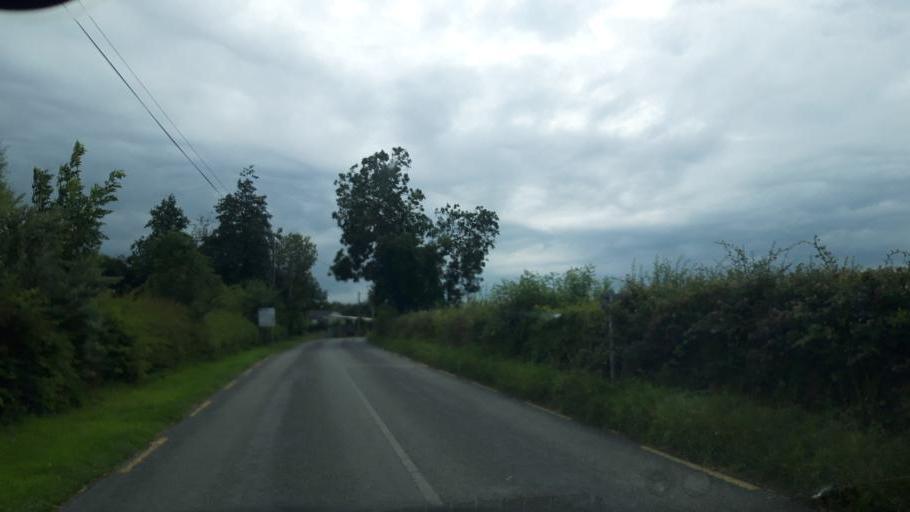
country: IE
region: Leinster
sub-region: Kilkenny
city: Ballyragget
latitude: 52.7444
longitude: -7.3958
